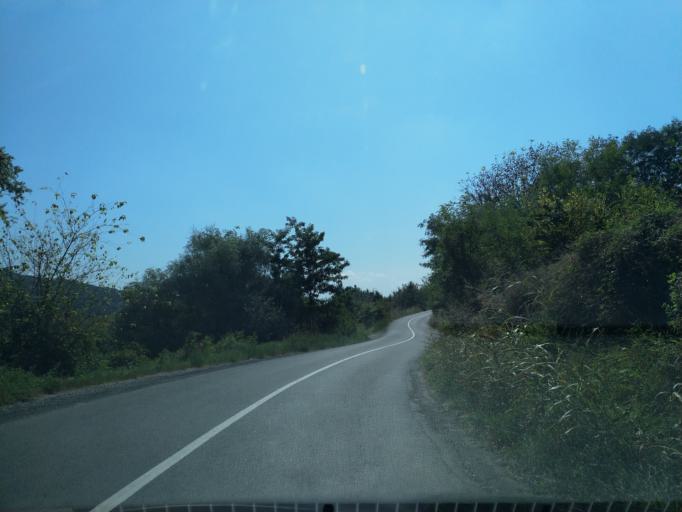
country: RS
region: Central Serbia
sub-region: Rasinski Okrug
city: Krusevac
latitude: 43.6319
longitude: 21.3727
